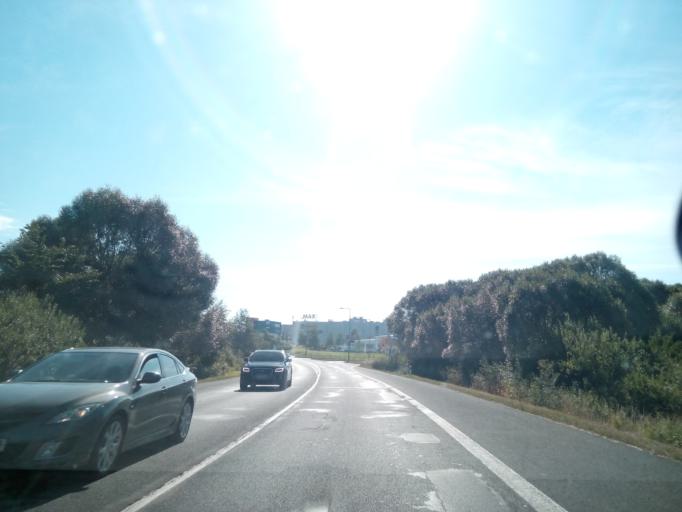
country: SK
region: Presovsky
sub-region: Okres Poprad
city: Poprad
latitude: 49.0510
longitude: 20.2851
